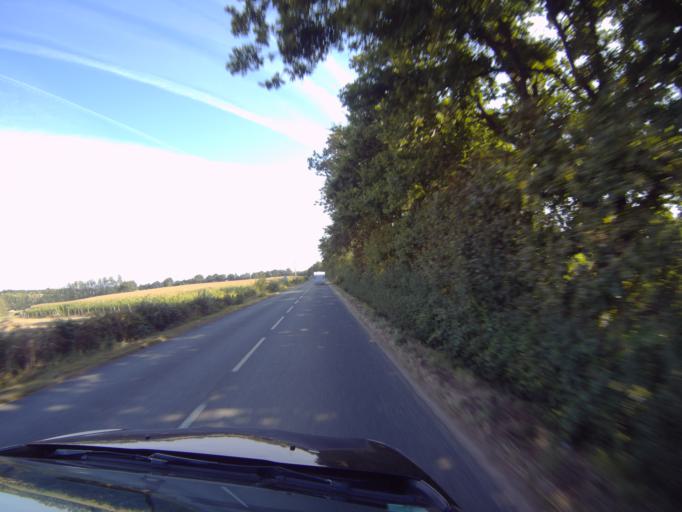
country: FR
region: Pays de la Loire
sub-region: Departement de la Vendee
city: Saint-Hilaire-de-Talmont
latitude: 46.4867
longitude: -1.5853
